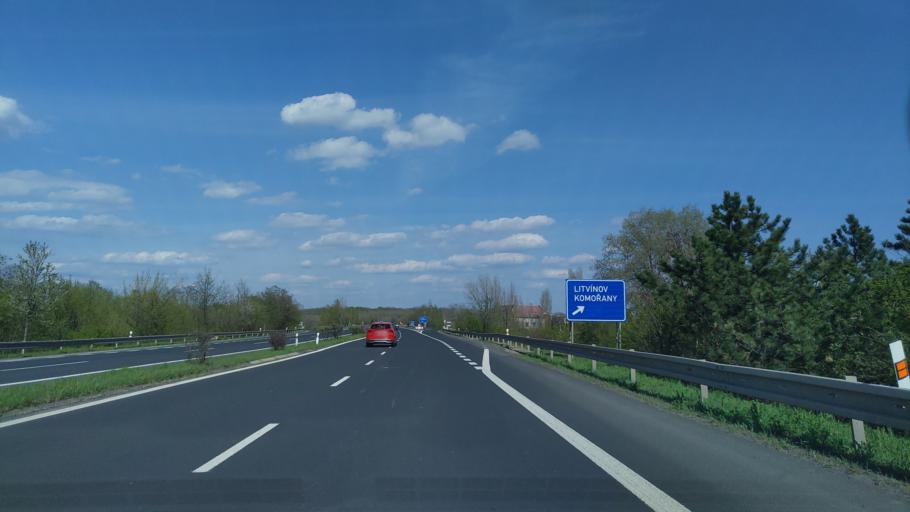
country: CZ
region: Ustecky
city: Horni Jiretin
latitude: 50.5259
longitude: 13.5651
